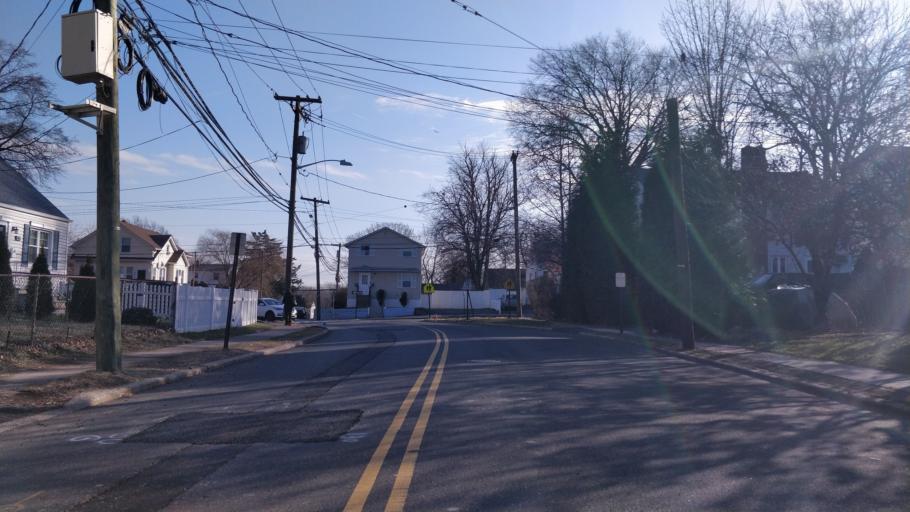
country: US
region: New Jersey
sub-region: Union County
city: Hillside
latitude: 40.7008
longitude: -74.2437
